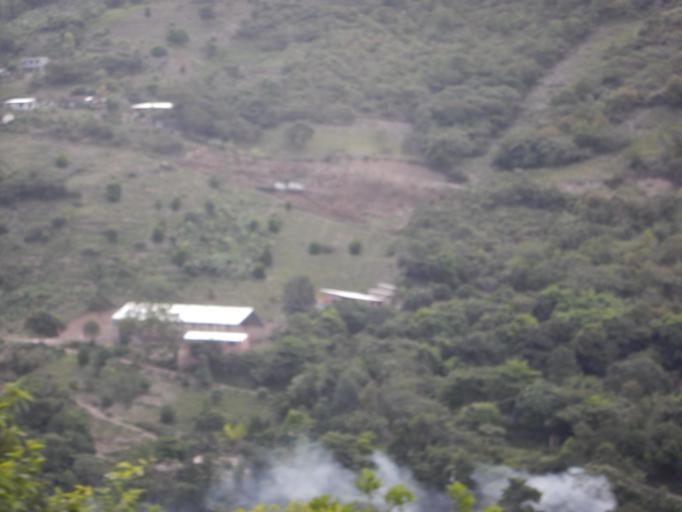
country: BO
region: La Paz
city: Coroico
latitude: -16.2259
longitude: -67.7406
